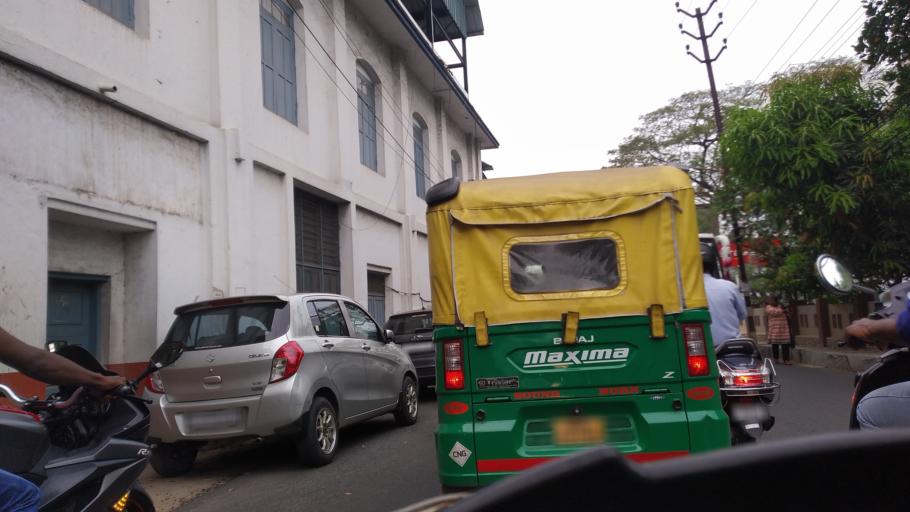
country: IN
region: Kerala
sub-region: Ernakulam
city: Cochin
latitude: 9.9397
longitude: 76.2962
